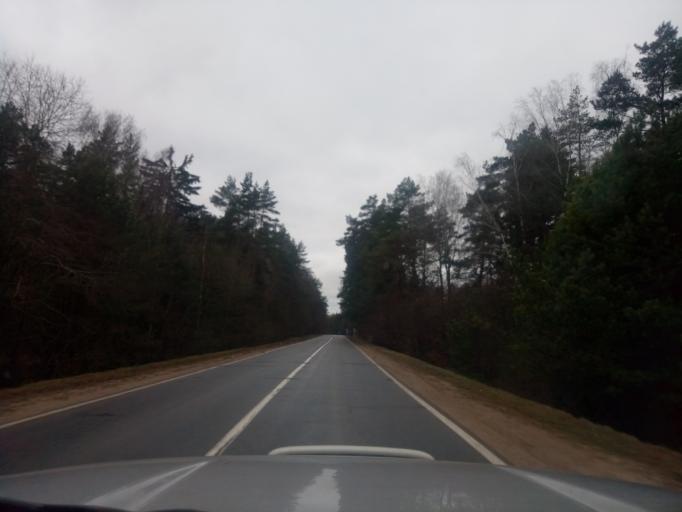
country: BY
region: Minsk
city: Kapyl'
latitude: 53.1606
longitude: 27.1134
